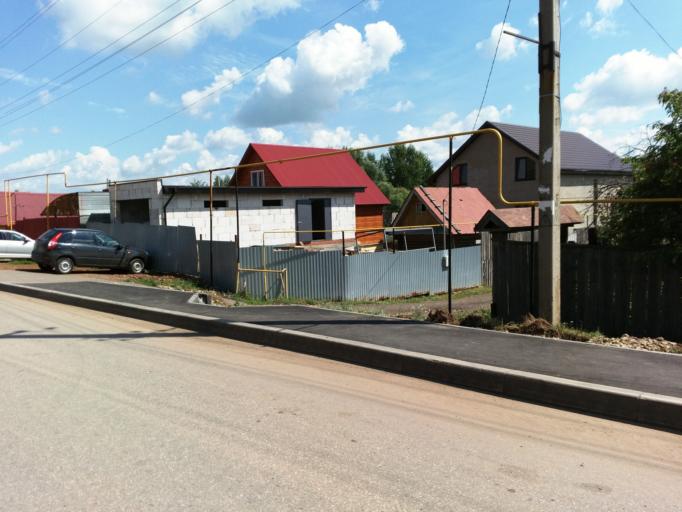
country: RU
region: Tatarstan
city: Yelabuga
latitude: 55.7493
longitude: 52.0381
